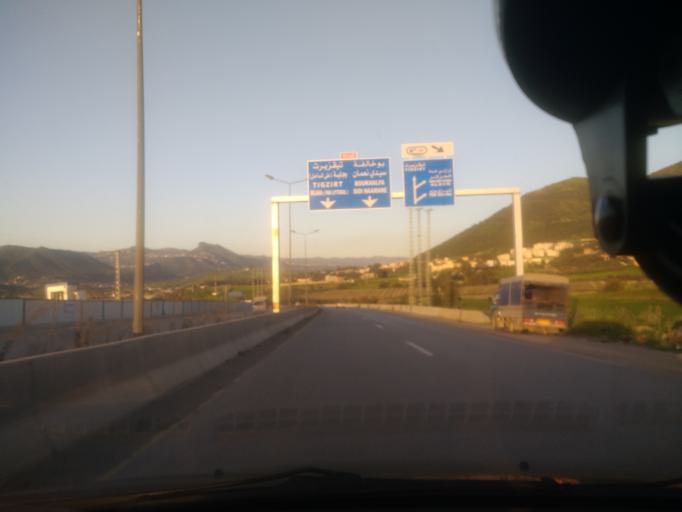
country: DZ
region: Boumerdes
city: Draa Ben Khedda
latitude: 36.7381
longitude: 4.0048
